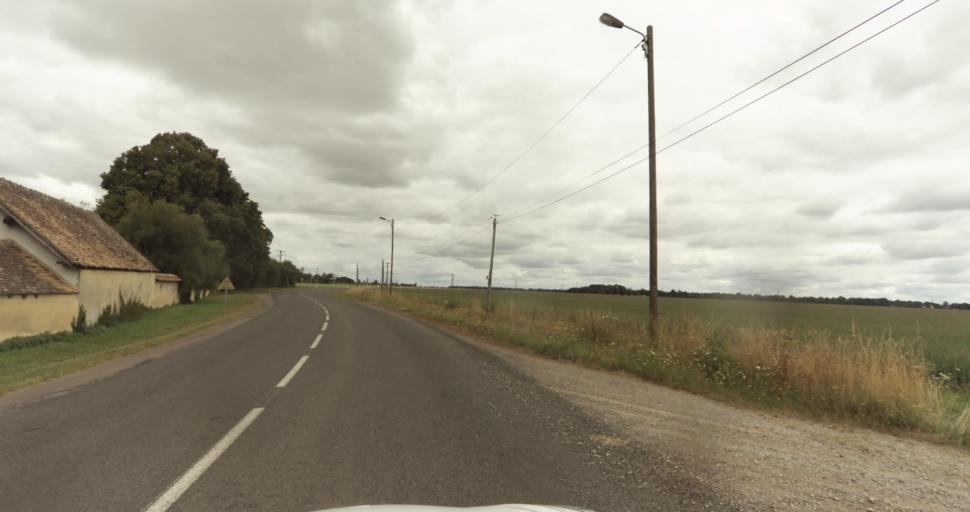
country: FR
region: Haute-Normandie
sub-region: Departement de l'Eure
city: La Madeleine-de-Nonancourt
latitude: 48.8296
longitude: 1.2278
